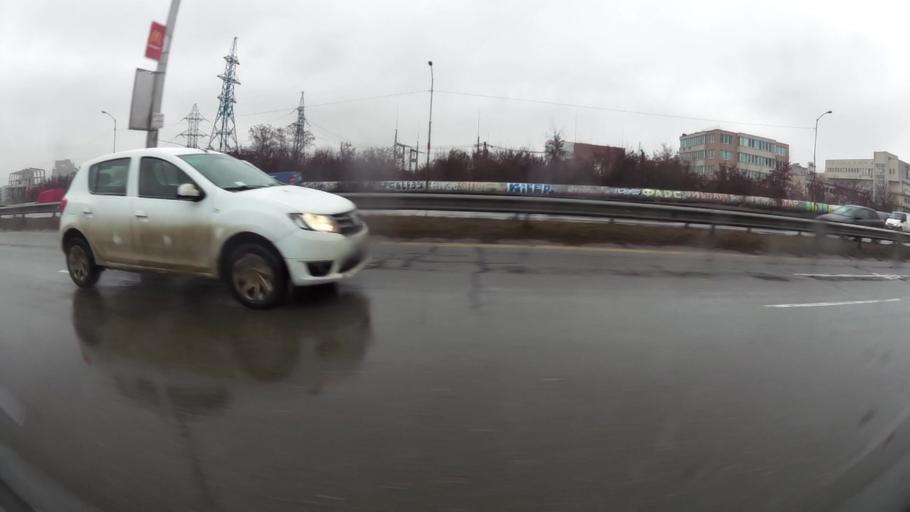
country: BG
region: Sofia-Capital
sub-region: Stolichna Obshtina
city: Sofia
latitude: 42.6591
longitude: 23.3875
